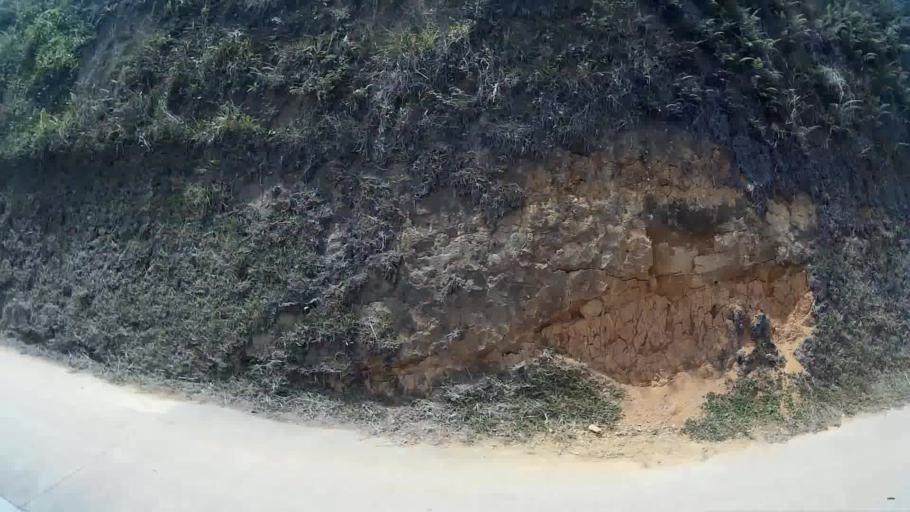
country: CO
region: Risaralda
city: Pereira
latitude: 4.8012
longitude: -75.7581
